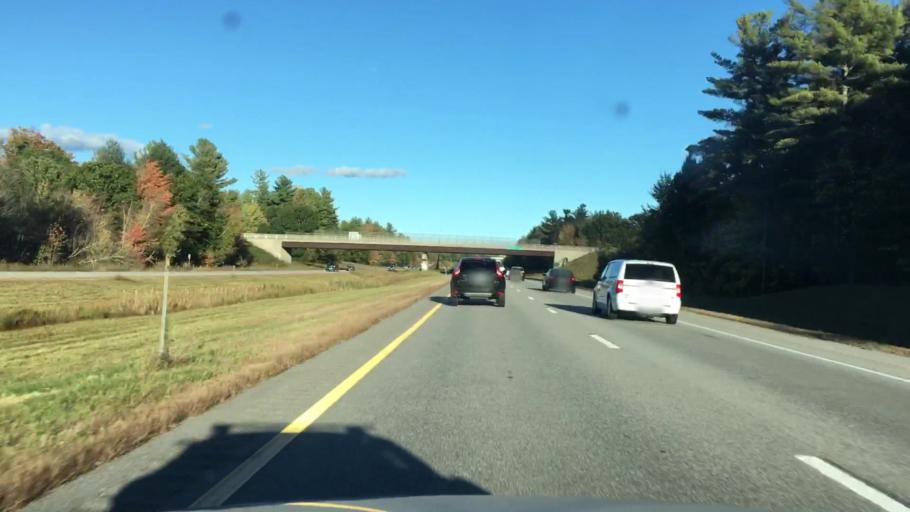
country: US
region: New Hampshire
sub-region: Rockingham County
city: Candia
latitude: 43.0413
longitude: -71.2834
